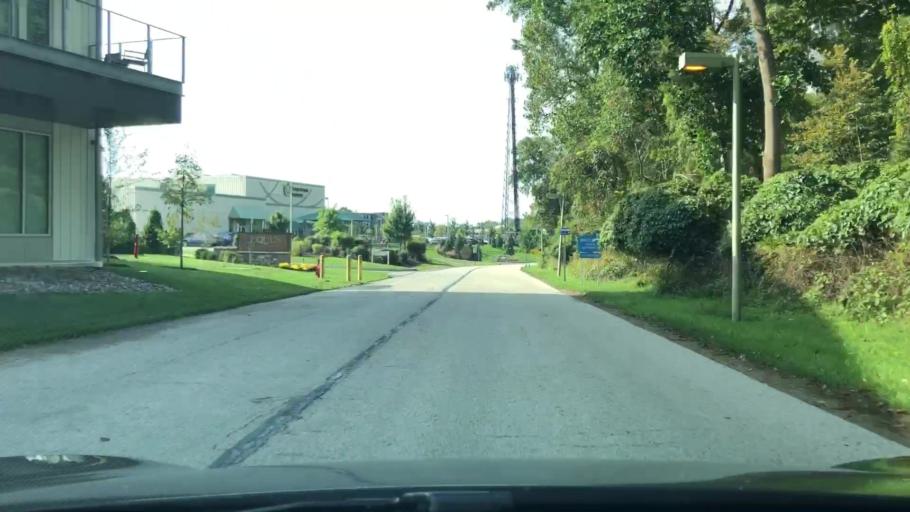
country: US
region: Pennsylvania
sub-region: Delaware County
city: Wayne
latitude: 39.9933
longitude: -75.4118
